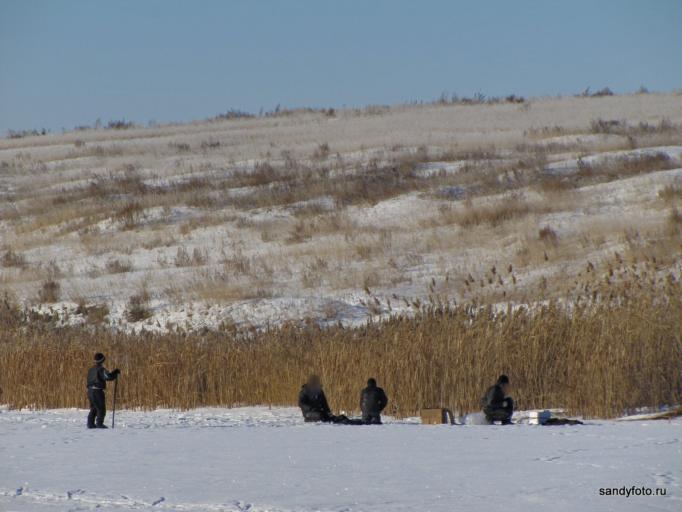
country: RU
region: Chelyabinsk
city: Troitsk
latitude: 54.0947
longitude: 61.5408
